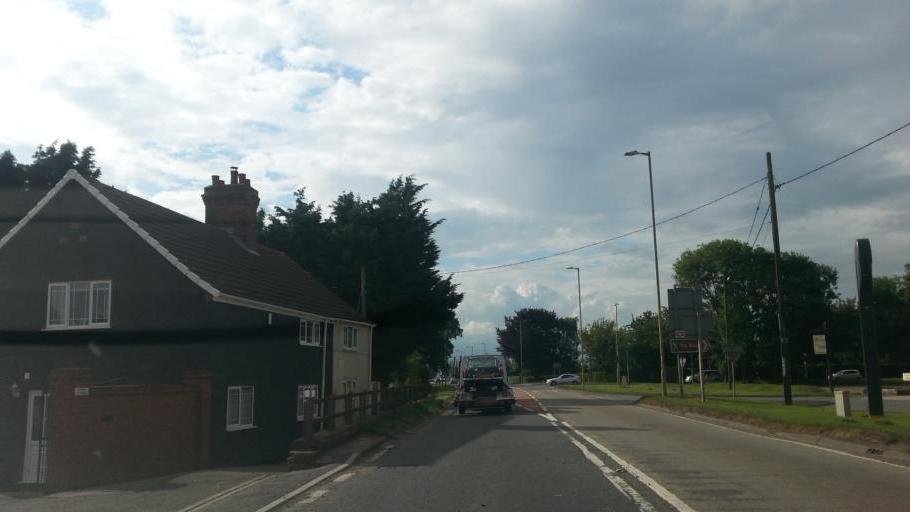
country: GB
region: England
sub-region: Lincolnshire
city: Donington
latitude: 52.9696
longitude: -0.1882
